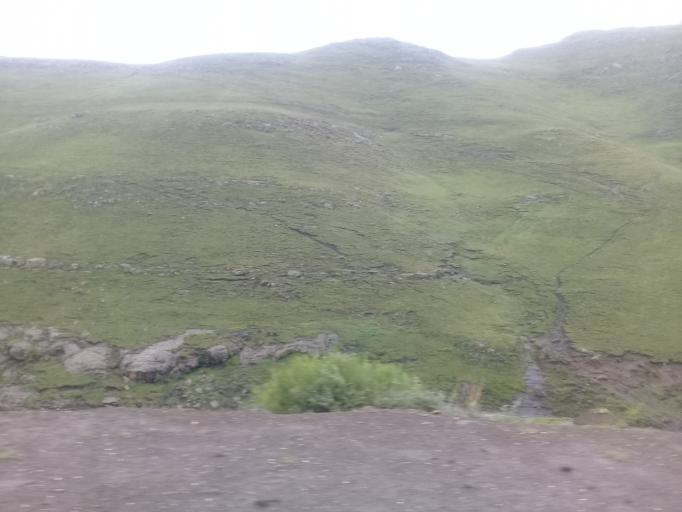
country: LS
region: Mokhotlong
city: Mokhotlong
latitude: -29.3879
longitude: 28.9571
